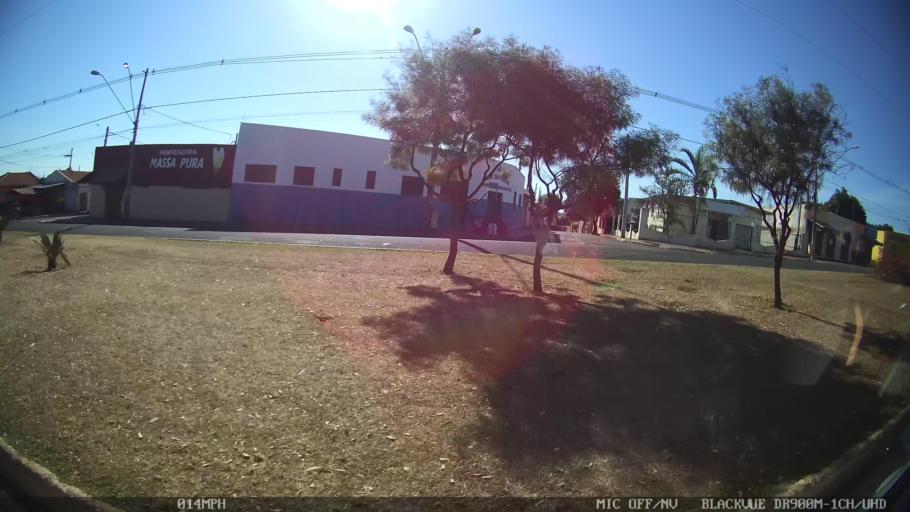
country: BR
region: Sao Paulo
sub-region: Olimpia
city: Olimpia
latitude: -20.7252
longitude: -48.9098
